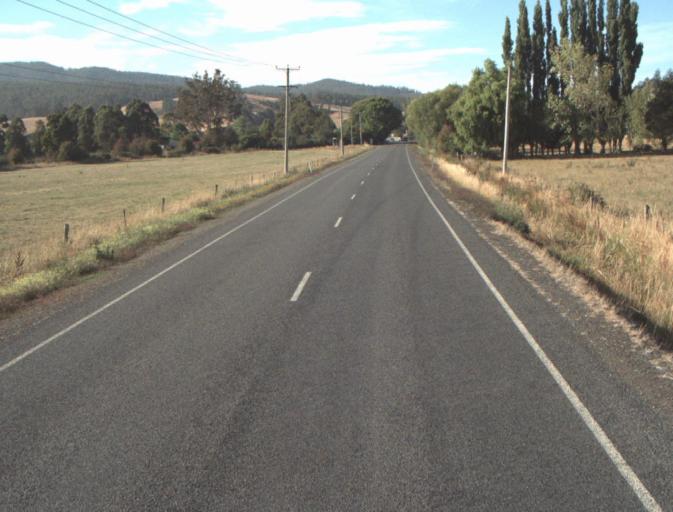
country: AU
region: Tasmania
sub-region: Launceston
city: Mayfield
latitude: -41.2455
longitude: 147.2172
